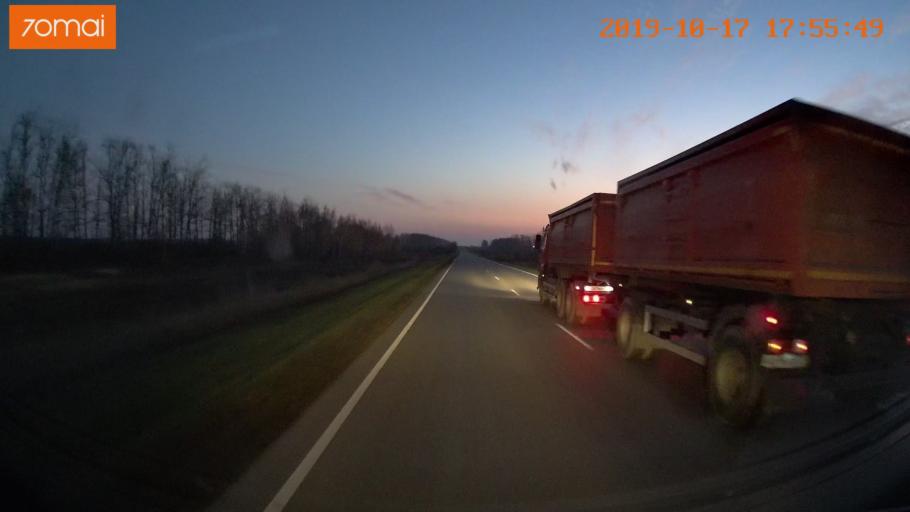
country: RU
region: Tula
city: Kurkino
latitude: 53.5888
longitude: 38.6544
